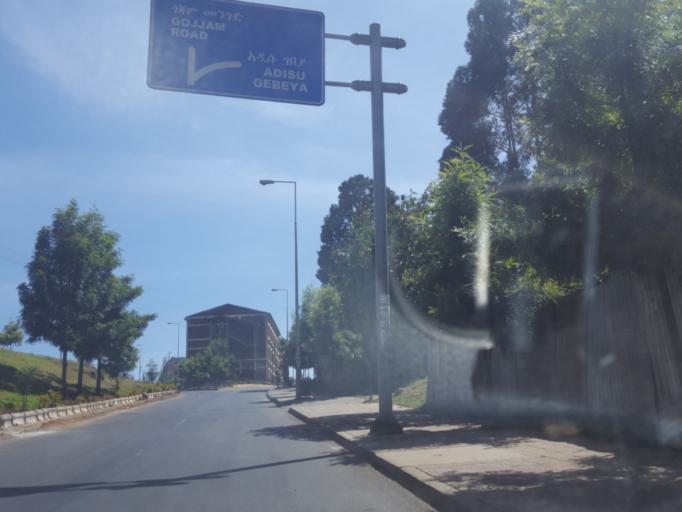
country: ET
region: Adis Abeba
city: Addis Ababa
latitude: 9.0639
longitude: 38.7292
